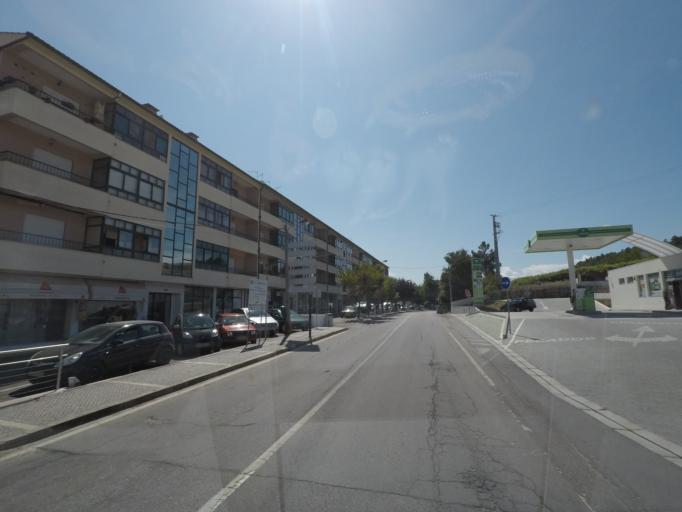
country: PT
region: Vila Real
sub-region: Sabrosa
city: Sabrosa
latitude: 41.2703
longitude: -7.4784
